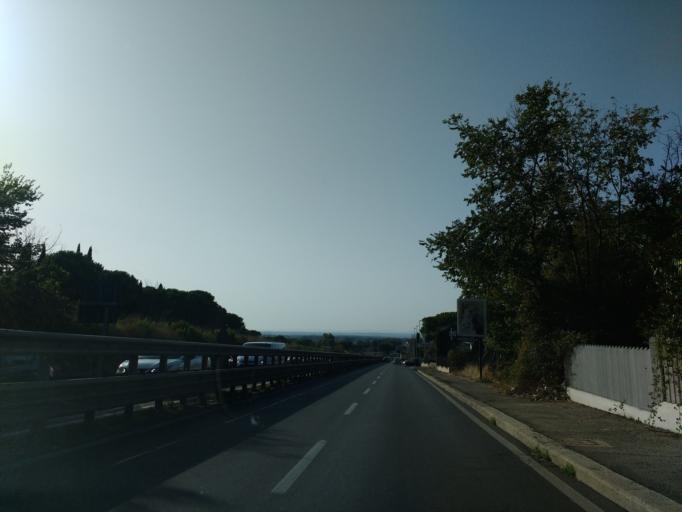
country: IT
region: Latium
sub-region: Citta metropolitana di Roma Capitale
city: Marino
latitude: 41.7692
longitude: 12.6143
